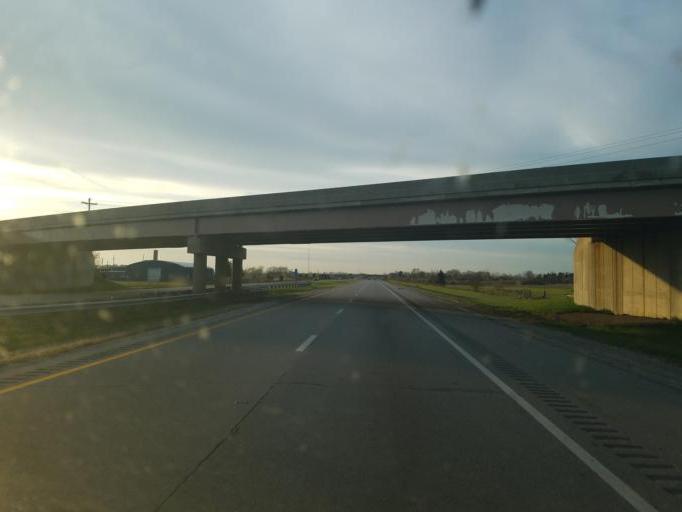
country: US
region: Ohio
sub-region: Wood County
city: Walbridge
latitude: 41.5728
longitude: -83.4679
